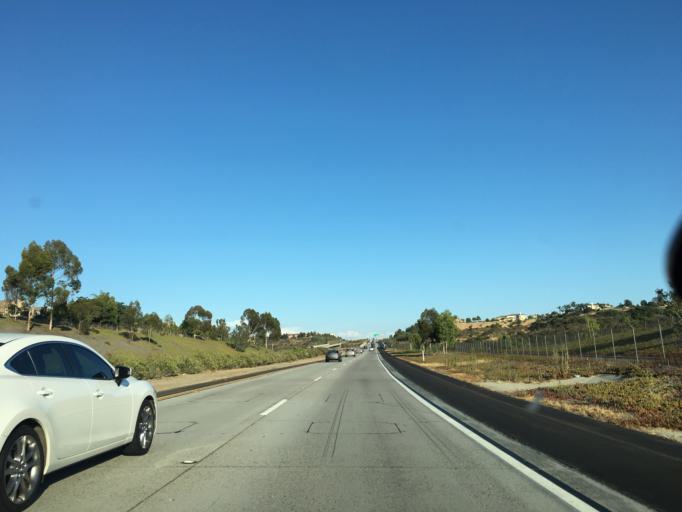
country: US
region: California
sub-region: San Diego County
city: Fairbanks Ranch
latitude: 32.9659
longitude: -117.1675
